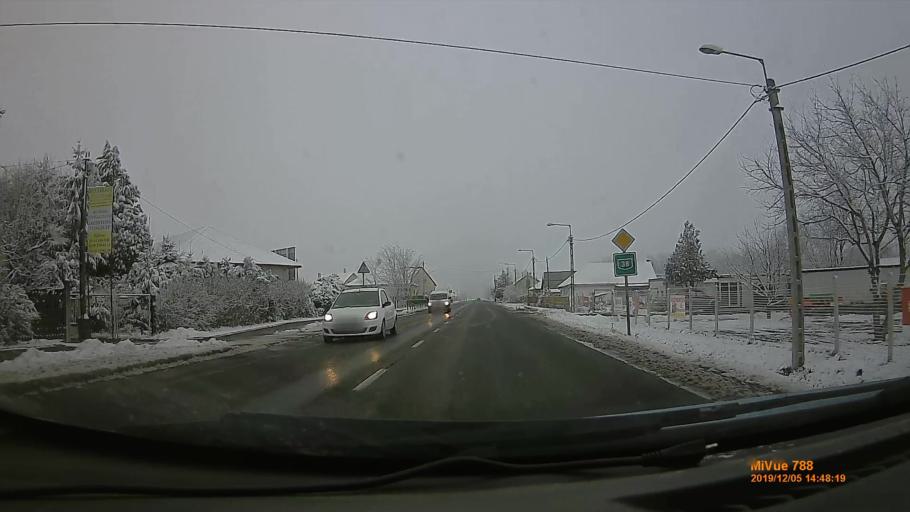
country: HU
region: Szabolcs-Szatmar-Bereg
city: Nyiregyhaza
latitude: 47.9753
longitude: 21.6889
